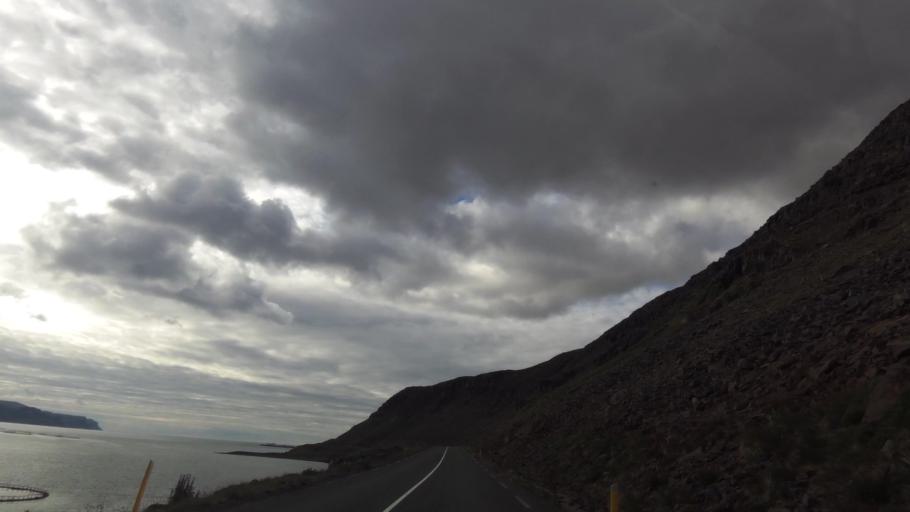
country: IS
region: West
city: Olafsvik
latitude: 65.5740
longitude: -23.9405
